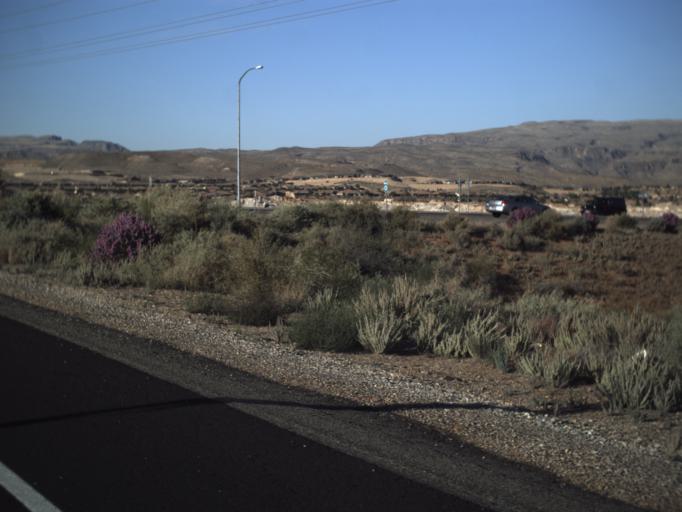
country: US
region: Utah
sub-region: Washington County
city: Saint George
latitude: 37.0287
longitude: -113.6054
